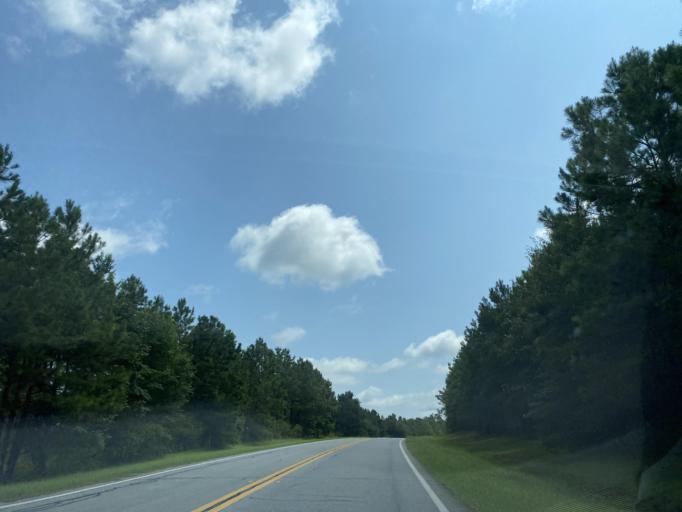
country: US
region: Georgia
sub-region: Wilcox County
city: Abbeville
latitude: 32.0055
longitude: -83.1656
